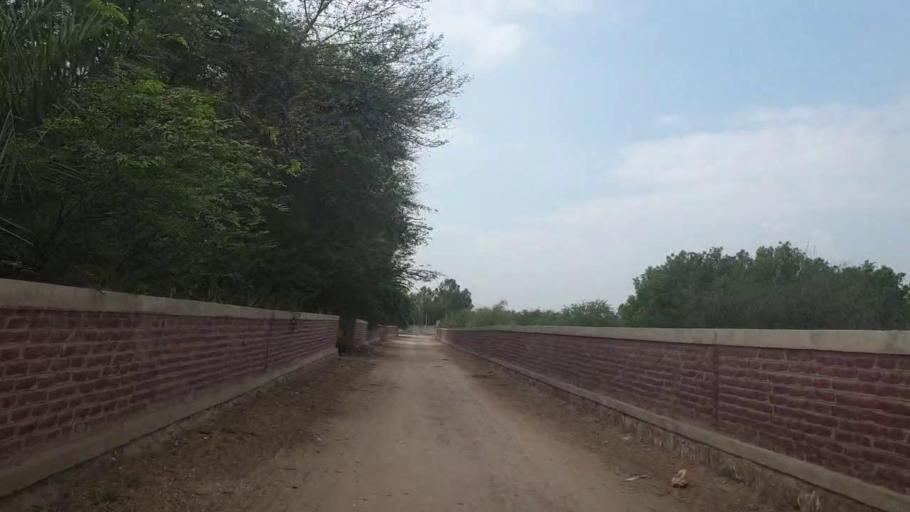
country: PK
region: Sindh
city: Sukkur
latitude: 27.6356
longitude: 68.7934
